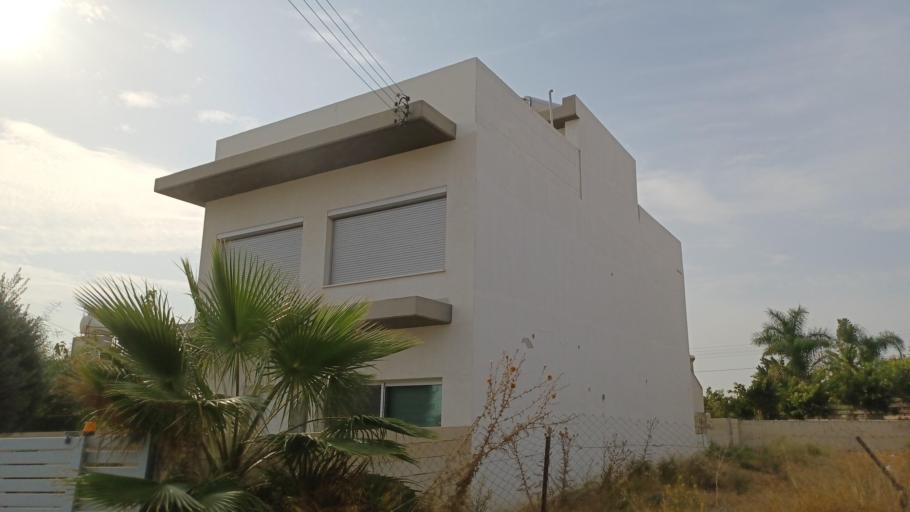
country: CY
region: Limassol
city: Ypsonas
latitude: 34.6953
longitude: 32.9471
